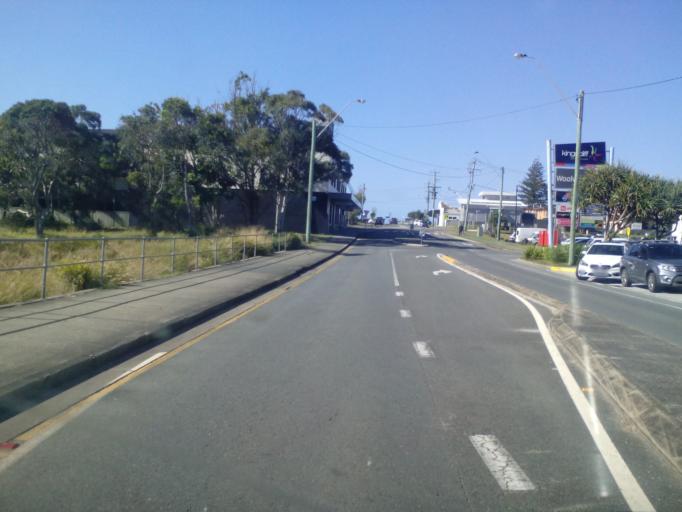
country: AU
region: New South Wales
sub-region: Tweed
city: Kingscliff
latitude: -28.2558
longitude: 153.5740
